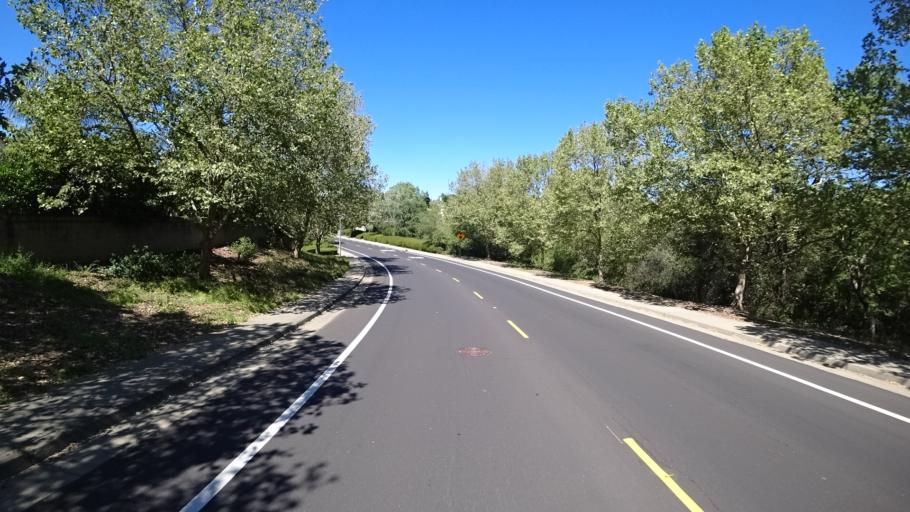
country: US
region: California
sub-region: Placer County
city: Rocklin
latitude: 38.7722
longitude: -121.2231
